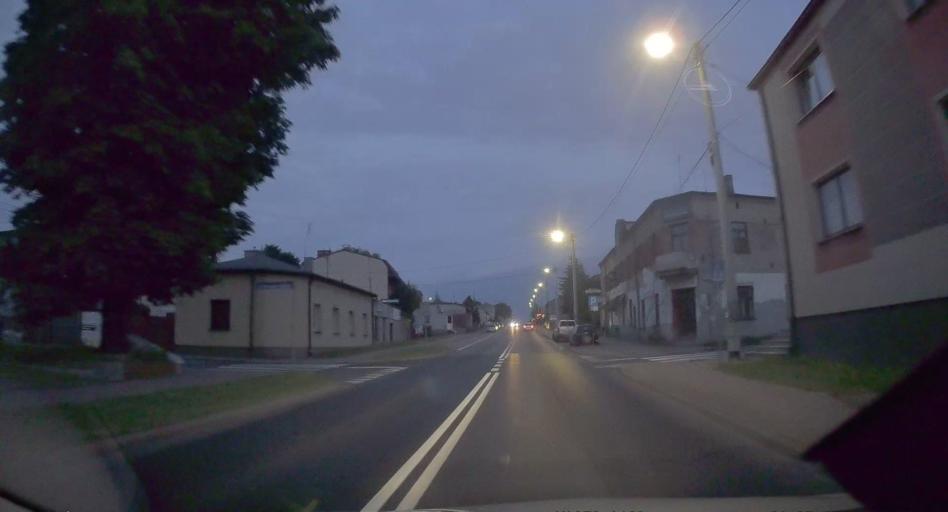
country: PL
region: Silesian Voivodeship
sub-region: Powiat klobucki
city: Klobuck
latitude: 50.9005
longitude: 18.9376
